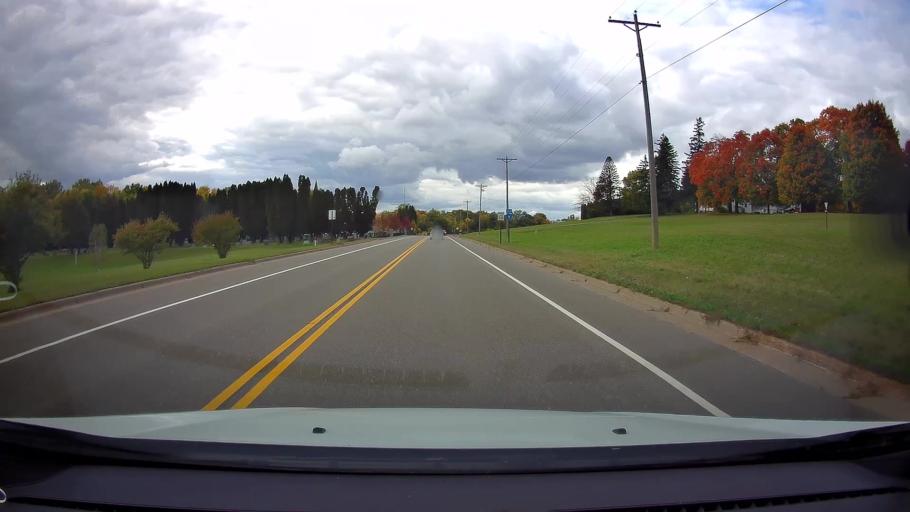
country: US
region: Minnesota
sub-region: Chisago County
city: Center City
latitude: 45.3981
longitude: -92.8127
